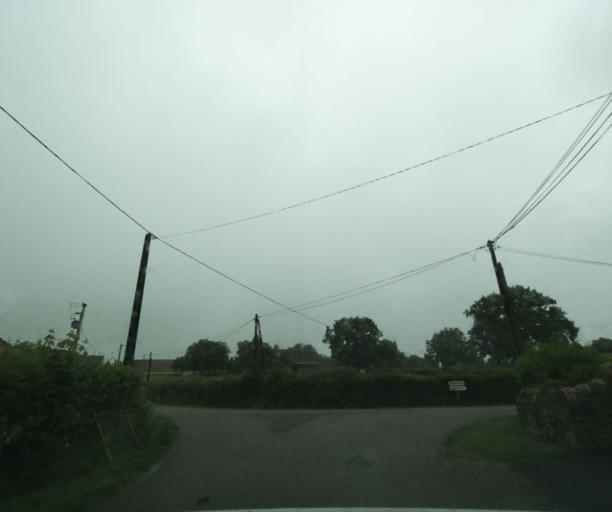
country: FR
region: Bourgogne
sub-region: Departement de Saone-et-Loire
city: Charolles
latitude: 46.4273
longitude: 4.3518
